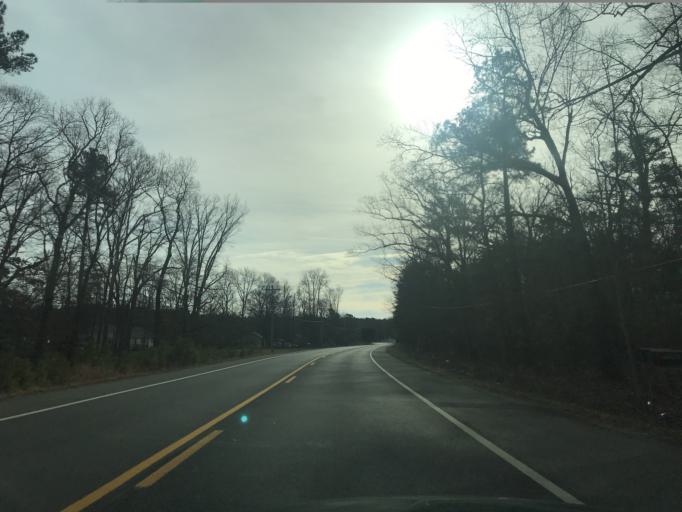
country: US
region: Maryland
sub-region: Charles County
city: Cobb Island
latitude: 38.2904
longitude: -76.8775
